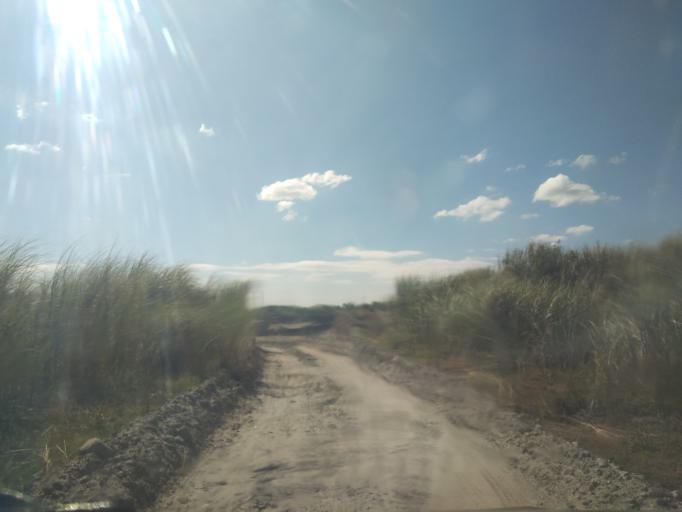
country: PH
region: Central Luzon
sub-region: Province of Pampanga
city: Calibutbut
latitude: 15.0814
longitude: 120.6050
